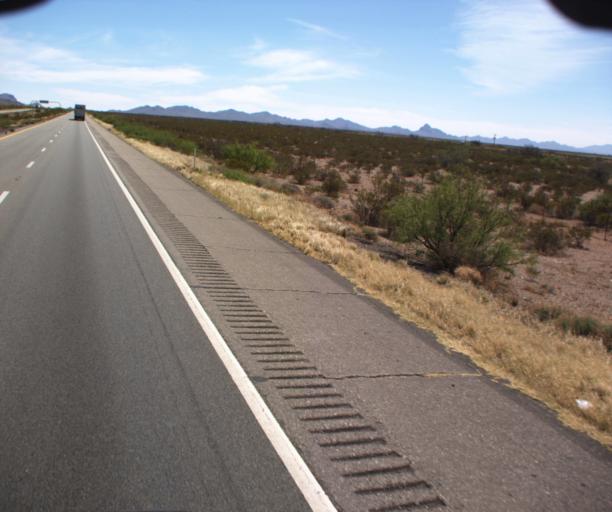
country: US
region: New Mexico
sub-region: Hidalgo County
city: Lordsburg
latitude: 32.2517
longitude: -109.1544
